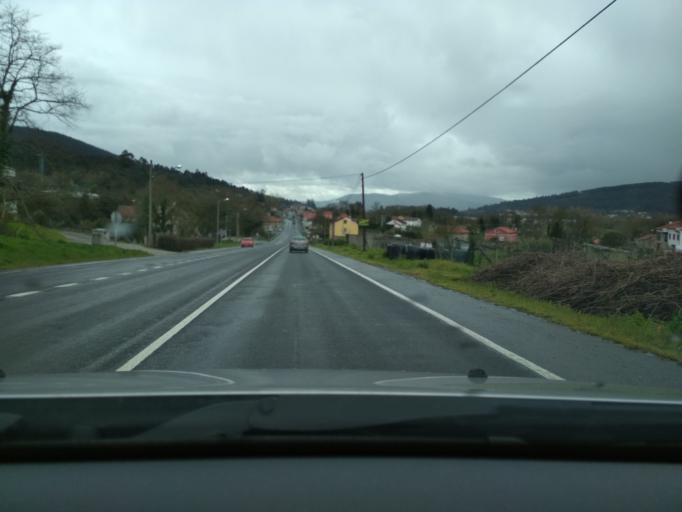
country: ES
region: Galicia
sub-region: Provincia da Coruna
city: Padron
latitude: 42.7724
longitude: -8.6520
